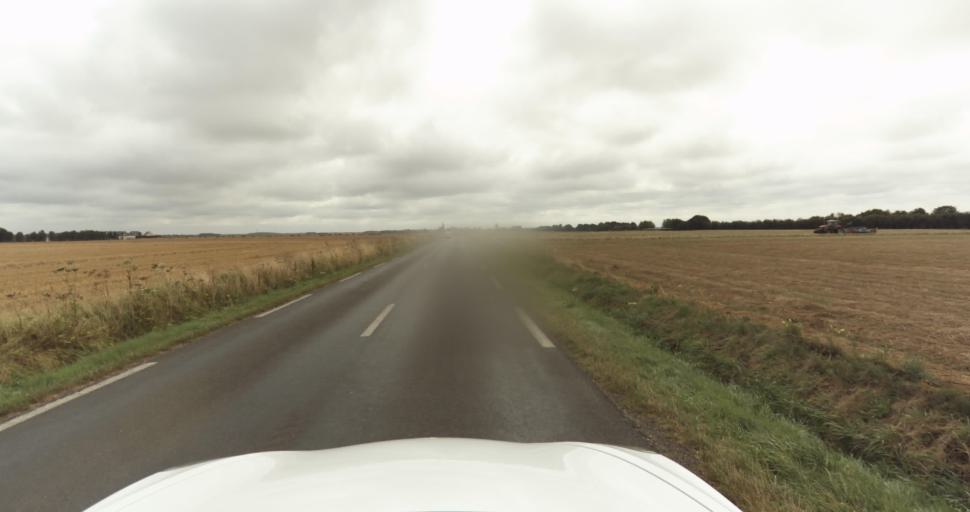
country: FR
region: Haute-Normandie
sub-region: Departement de l'Eure
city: Claville
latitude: 49.0788
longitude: 1.0581
